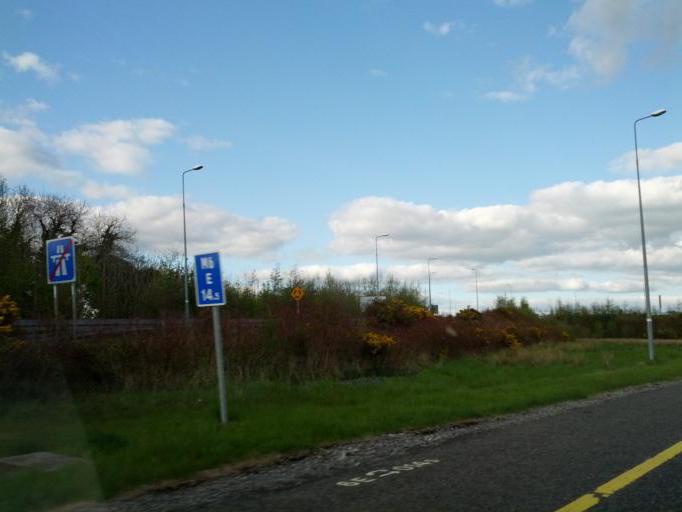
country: IE
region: Leinster
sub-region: An Iarmhi
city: Rochfortbridge
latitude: 53.4042
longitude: -7.2867
